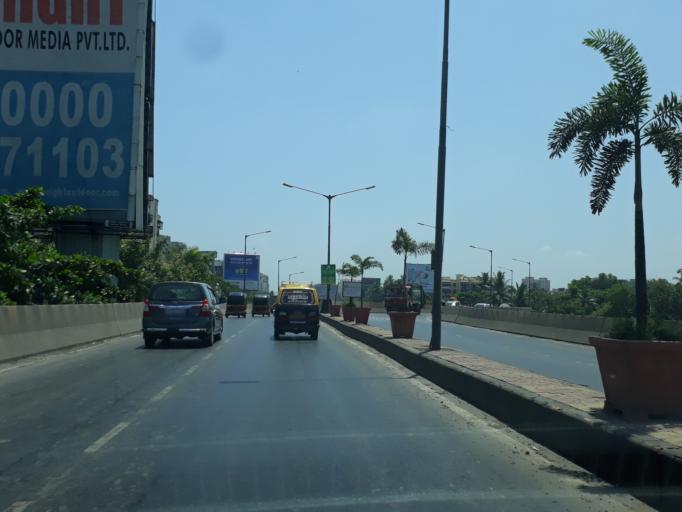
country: IN
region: Maharashtra
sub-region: Mumbai Suburban
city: Mumbai
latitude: 19.0670
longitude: 72.9011
